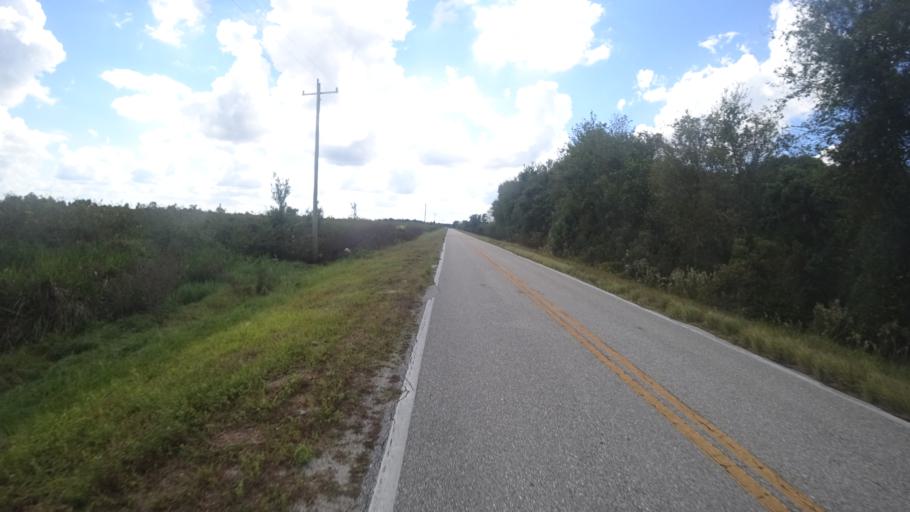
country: US
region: Florida
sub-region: DeSoto County
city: Arcadia
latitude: 27.3131
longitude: -82.1096
